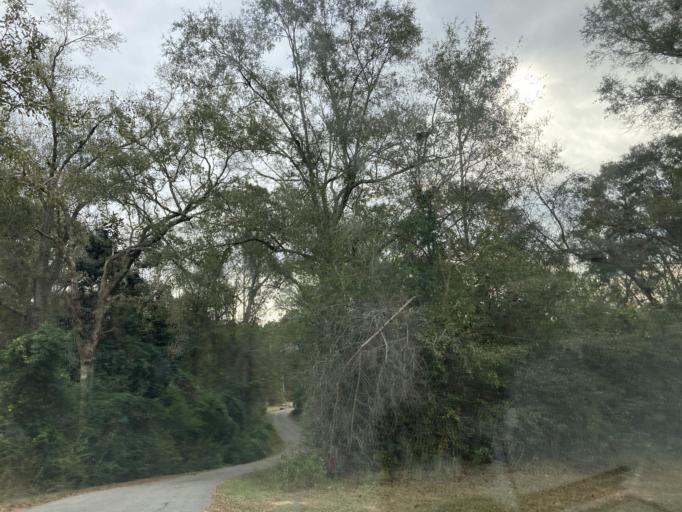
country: US
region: Mississippi
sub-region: Lamar County
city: Purvis
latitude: 31.1586
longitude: -89.4568
